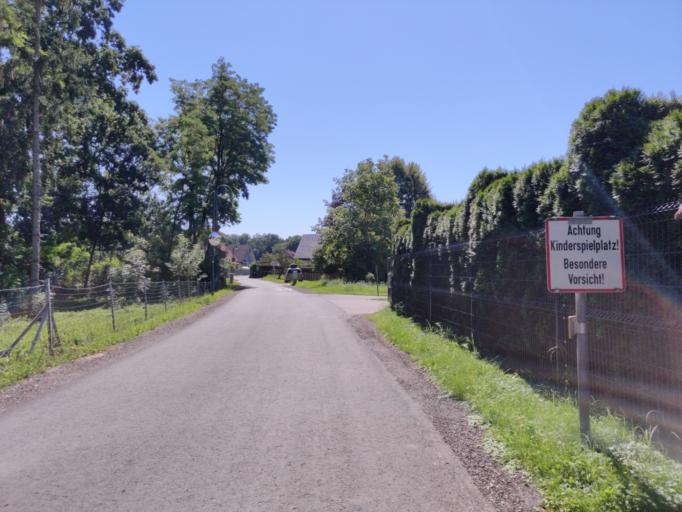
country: AT
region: Styria
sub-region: Politischer Bezirk Leibnitz
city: Lang
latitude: 46.8452
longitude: 15.5411
